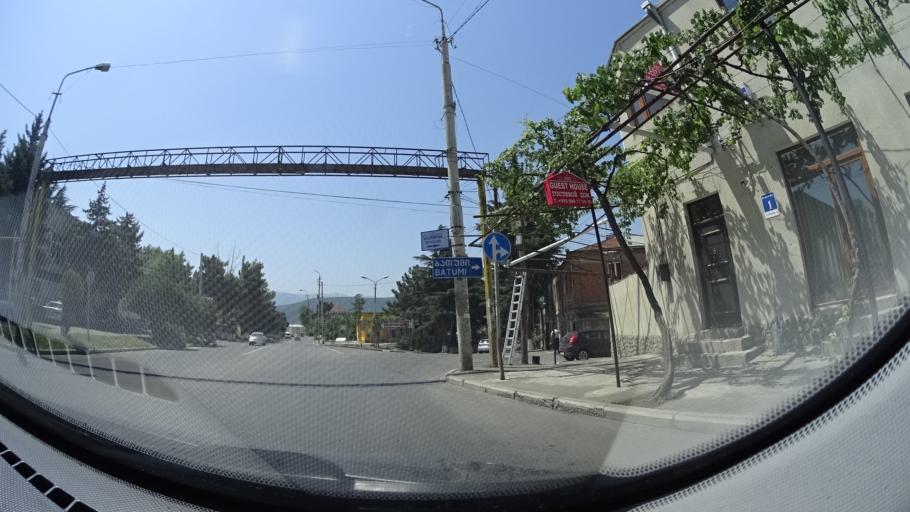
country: GE
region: Shida Kartli
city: Gori
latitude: 41.9935
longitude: 44.1224
